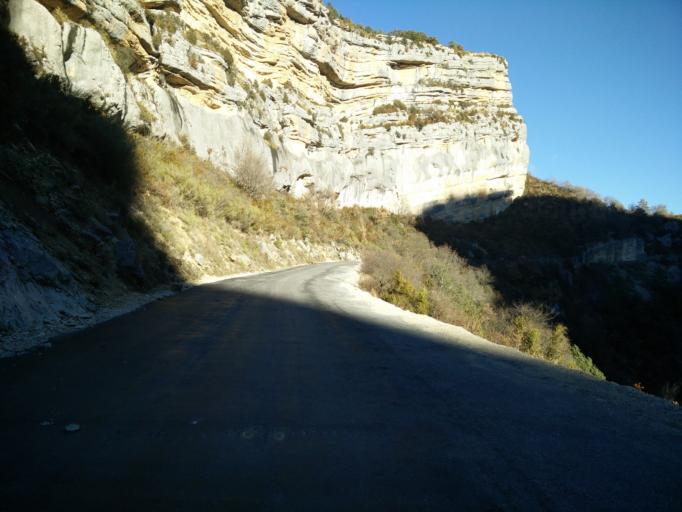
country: FR
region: Provence-Alpes-Cote d'Azur
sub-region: Departement des Alpes-de-Haute-Provence
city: Castellane
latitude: 43.7897
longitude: 6.3958
